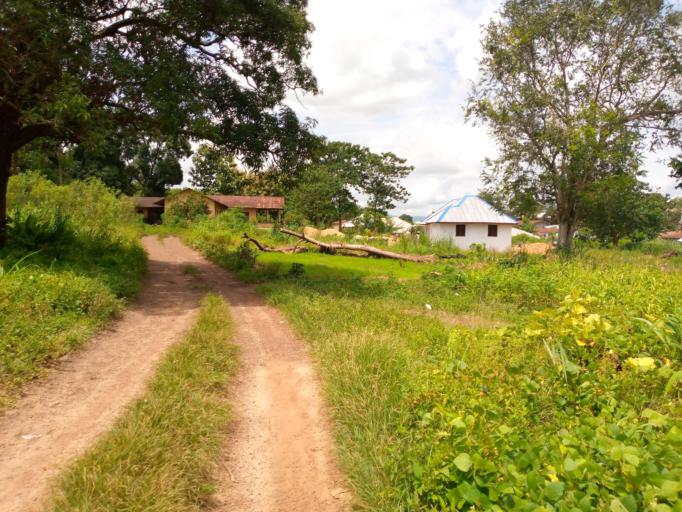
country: SL
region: Northern Province
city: Magburaka
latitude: 8.7232
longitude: -11.9345
